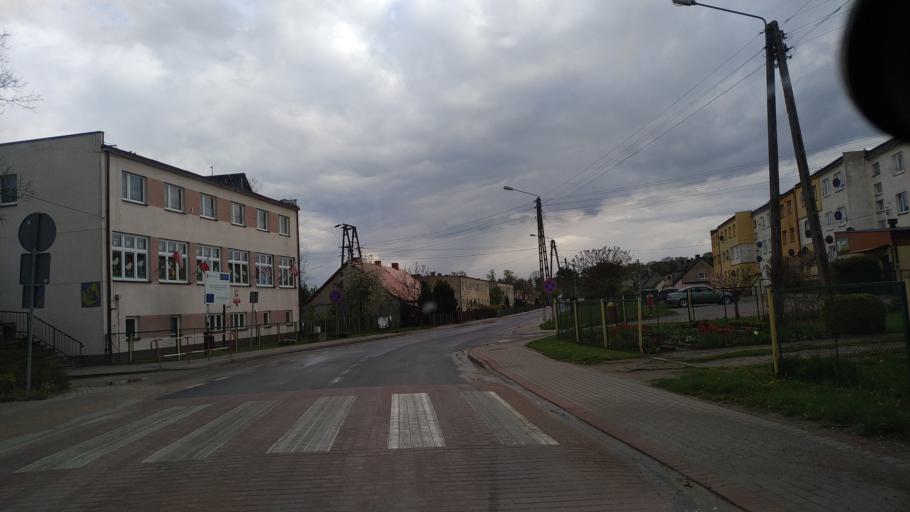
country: PL
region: Pomeranian Voivodeship
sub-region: Powiat starogardzki
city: Smetowo Graniczne
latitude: 53.7401
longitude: 18.6508
